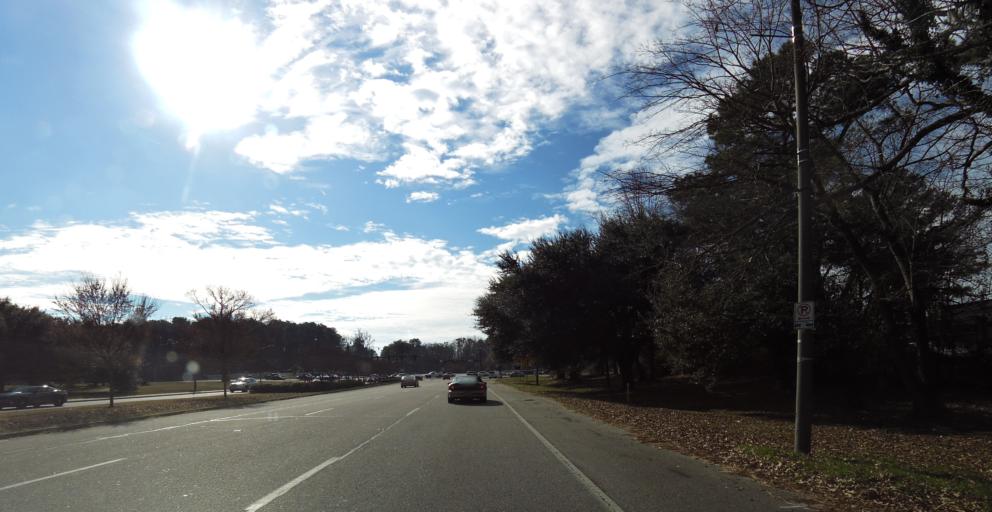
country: US
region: Virginia
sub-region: City of Newport News
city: Newport News
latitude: 37.0629
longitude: -76.4864
